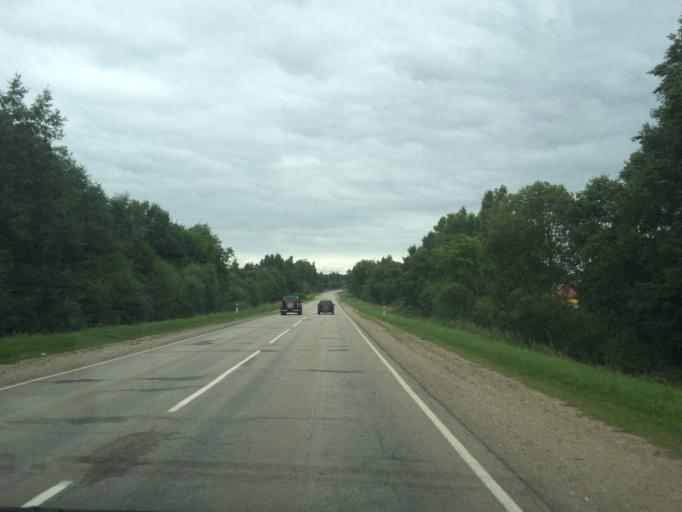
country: LV
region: Rezekne
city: Rezekne
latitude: 56.5635
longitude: 27.3658
